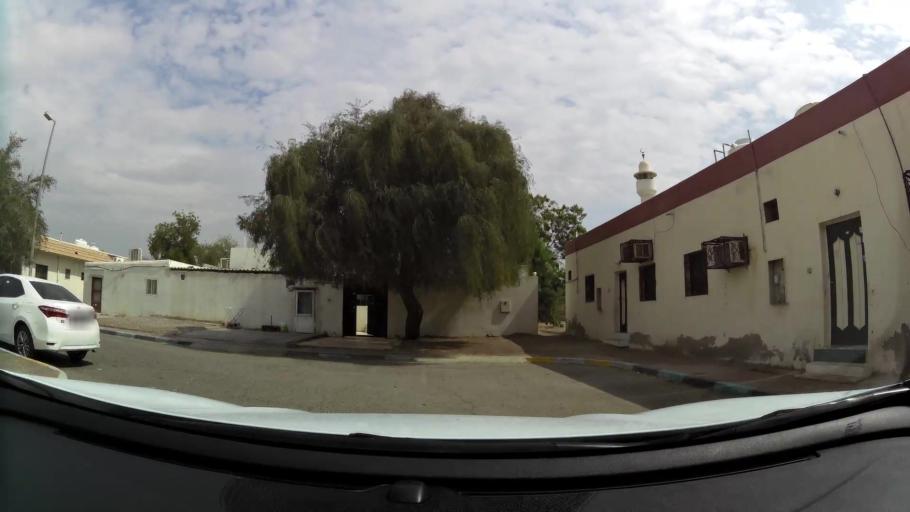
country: AE
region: Abu Dhabi
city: Al Ain
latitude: 24.2138
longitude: 55.7853
